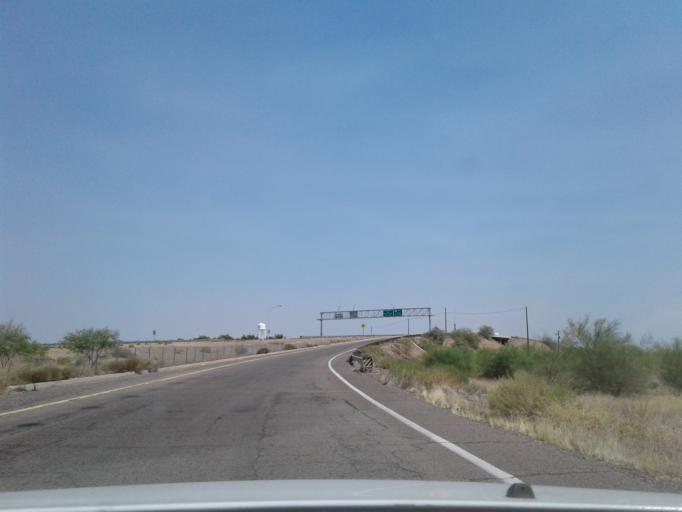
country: US
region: Arizona
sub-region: Pinal County
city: Eloy
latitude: 32.7243
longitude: -111.5147
